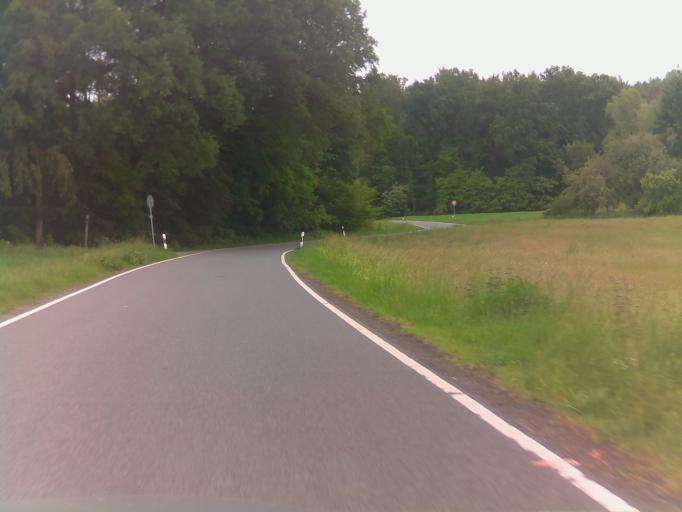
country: DE
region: Bavaria
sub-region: Regierungsbezirk Unterfranken
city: Johannesberg
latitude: 50.0064
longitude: 9.1182
